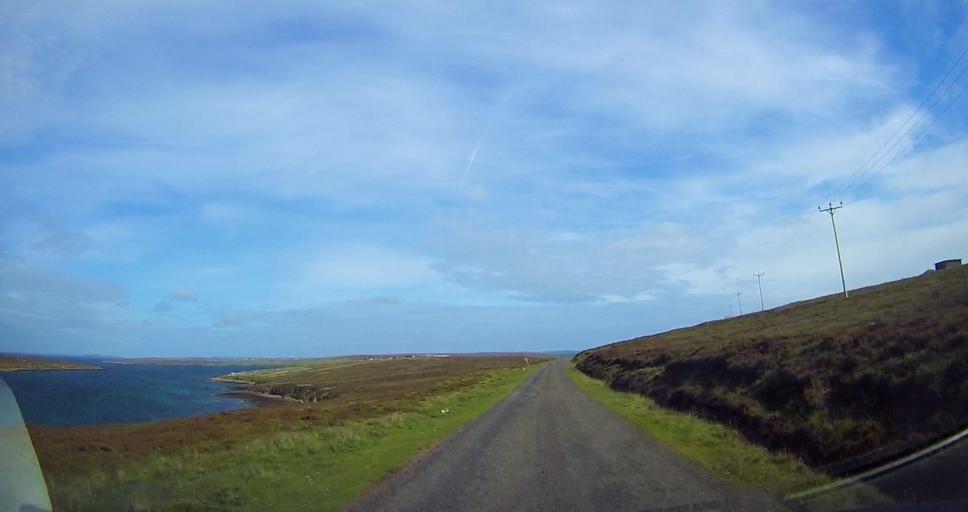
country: GB
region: Scotland
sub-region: Orkney Islands
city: Stromness
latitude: 58.8582
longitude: -3.2166
